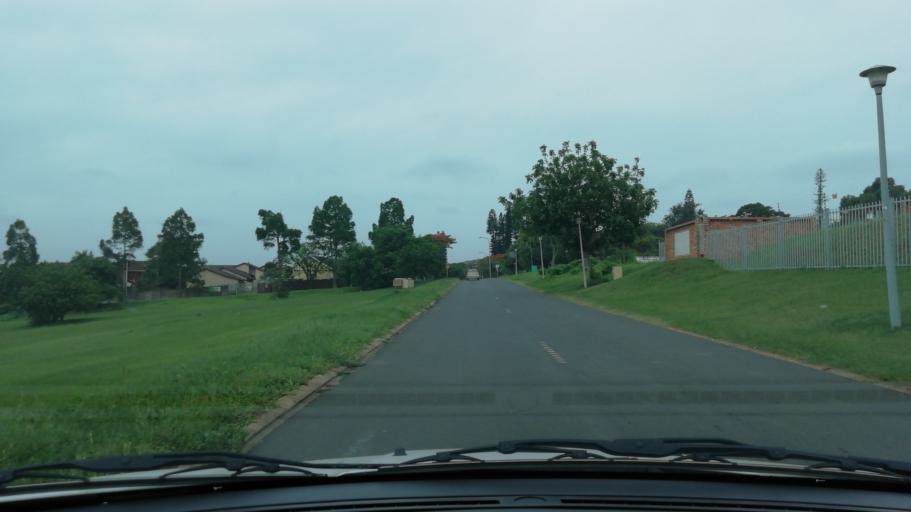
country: ZA
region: KwaZulu-Natal
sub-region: uThungulu District Municipality
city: Empangeni
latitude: -28.7411
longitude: 31.8868
